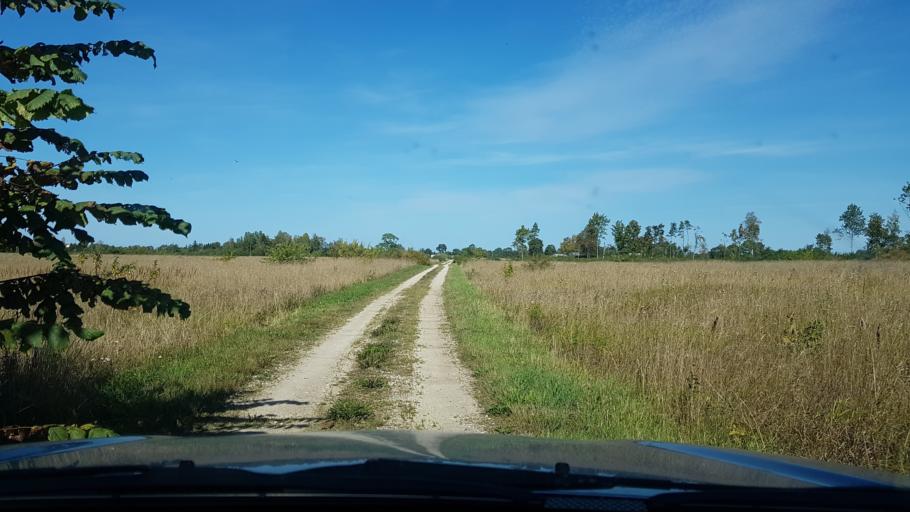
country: EE
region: Ida-Virumaa
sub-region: Sillamaee linn
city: Sillamae
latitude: 59.3775
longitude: 27.8106
